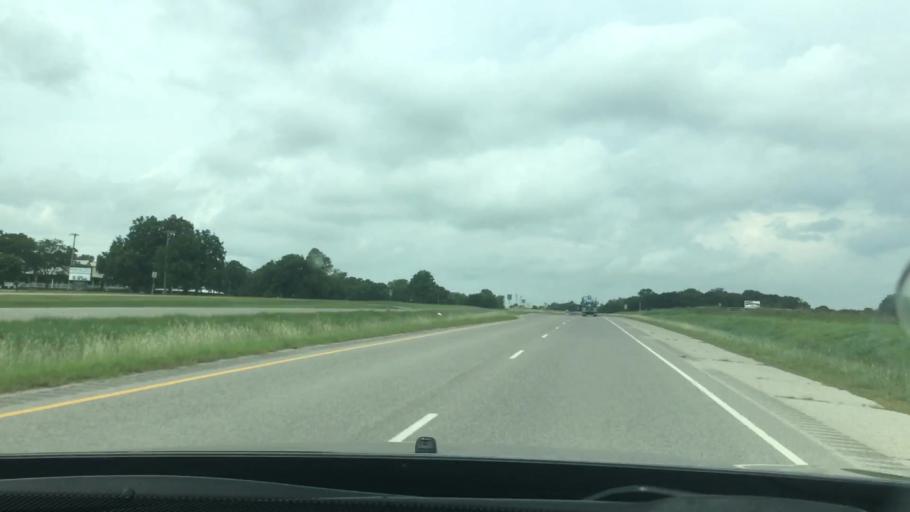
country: US
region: Oklahoma
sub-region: Carter County
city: Wilson
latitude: 34.1732
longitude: -97.4247
